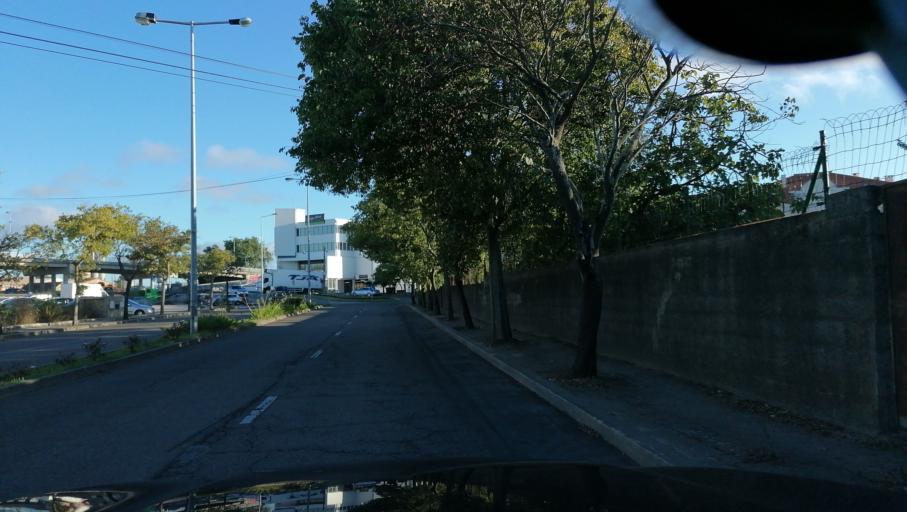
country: PT
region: Aveiro
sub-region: Aveiro
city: Aradas
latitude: 40.6317
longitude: -8.6435
